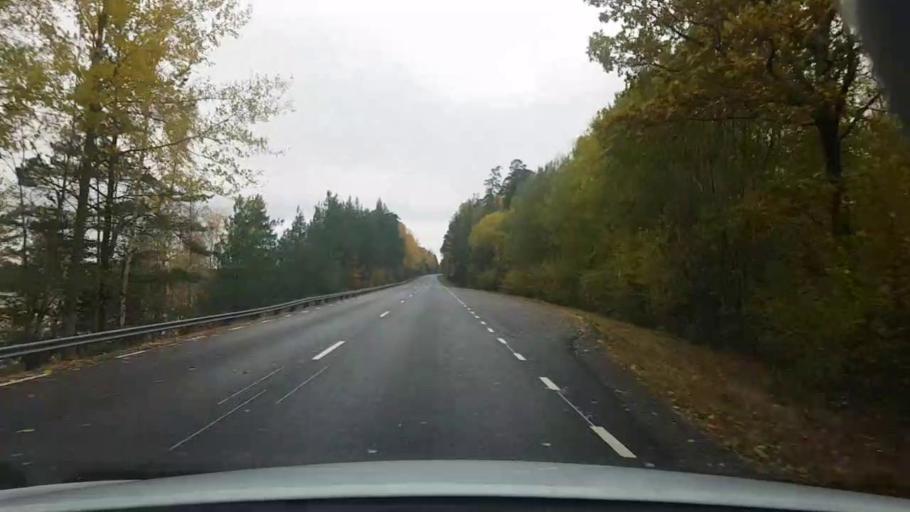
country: SE
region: OErebro
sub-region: Laxa Kommun
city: Laxa
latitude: 58.8371
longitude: 14.5469
